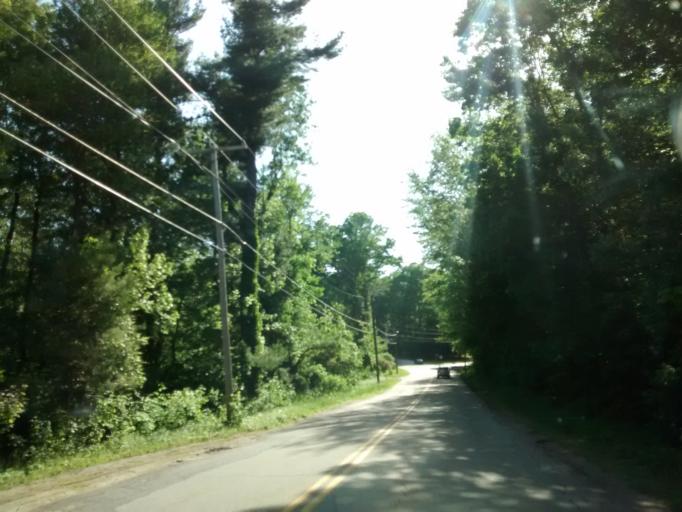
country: US
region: Massachusetts
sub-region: Worcester County
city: Charlton
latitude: 42.1647
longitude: -71.9619
